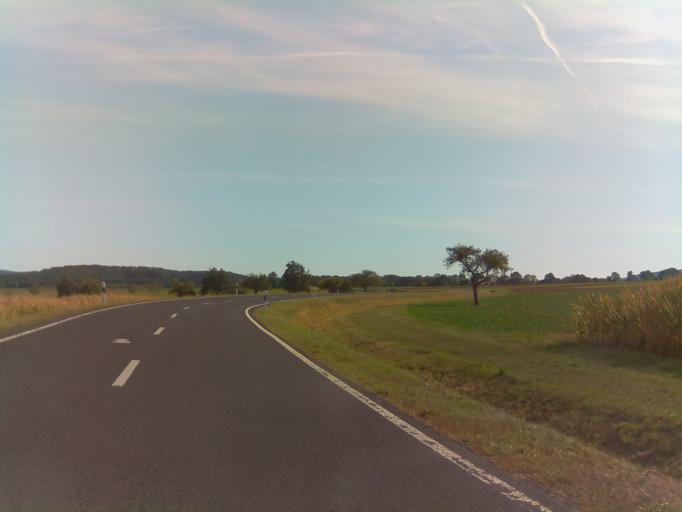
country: DE
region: Bavaria
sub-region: Regierungsbezirk Unterfranken
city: Fladungen
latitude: 50.5139
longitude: 10.1491
